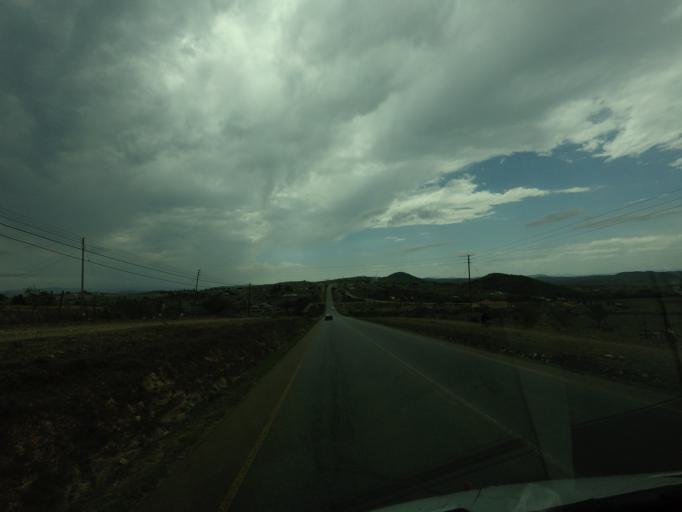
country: SZ
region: Manzini
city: Manzini
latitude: -26.5113
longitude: 31.5198
